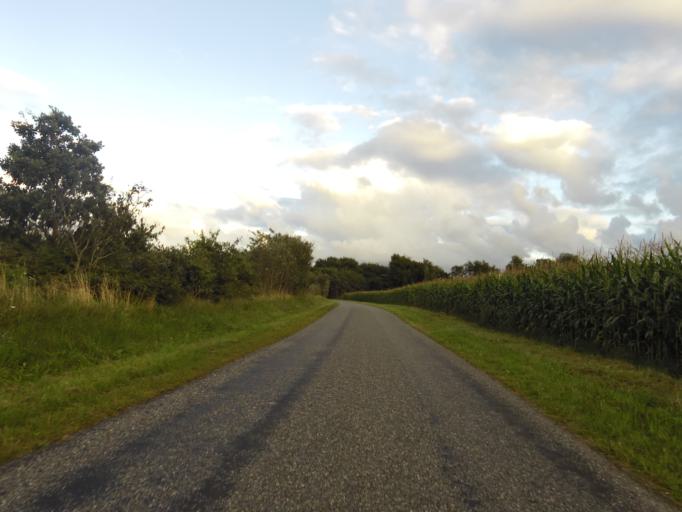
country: DK
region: South Denmark
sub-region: Esbjerg Kommune
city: Ribe
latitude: 55.3044
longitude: 8.7765
